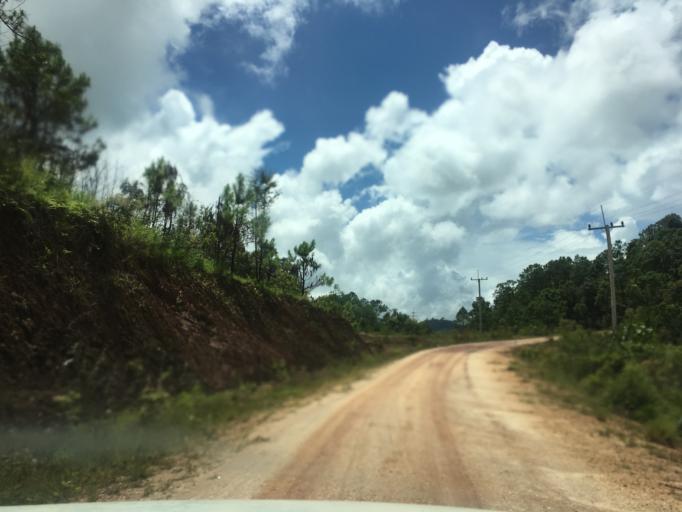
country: LA
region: Xiangkhoang
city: Phonsavan
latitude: 19.6740
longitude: 103.0804
